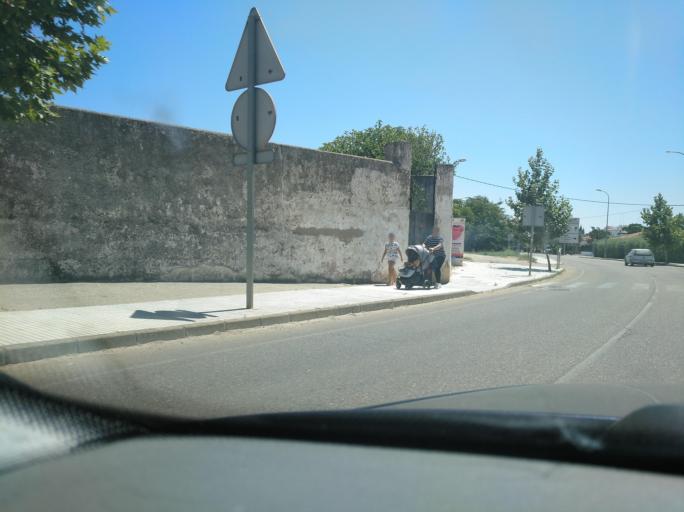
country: ES
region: Extremadura
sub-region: Provincia de Badajoz
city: Olivenza
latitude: 38.6895
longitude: -7.0979
